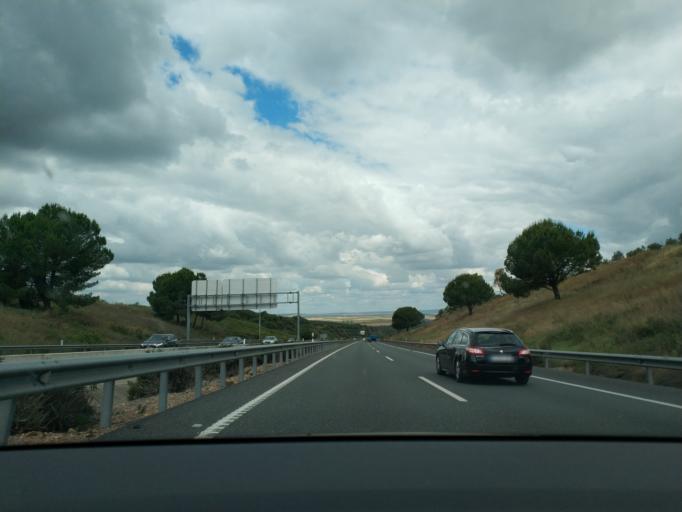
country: ES
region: Andalusia
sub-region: Provincia de Sevilla
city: Benacazon
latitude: 37.3630
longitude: -6.2079
